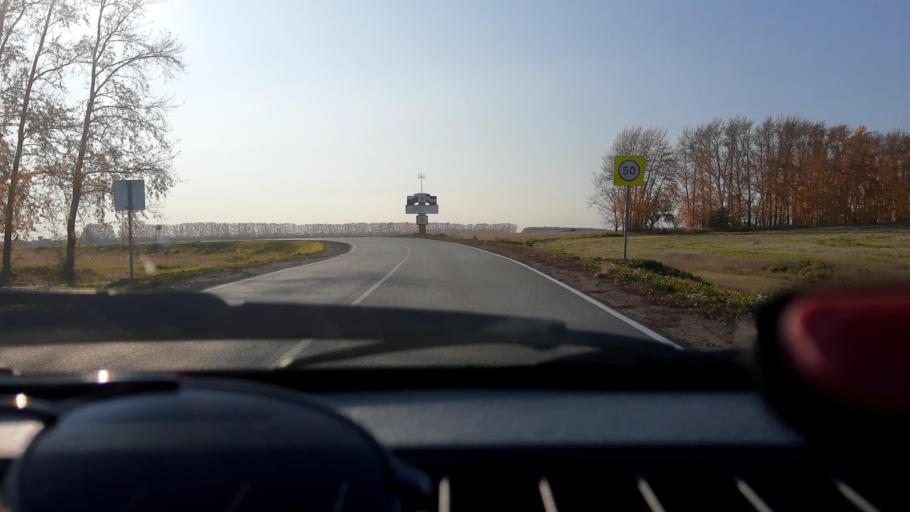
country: RU
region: Bashkortostan
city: Kabakovo
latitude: 54.4755
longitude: 55.9597
